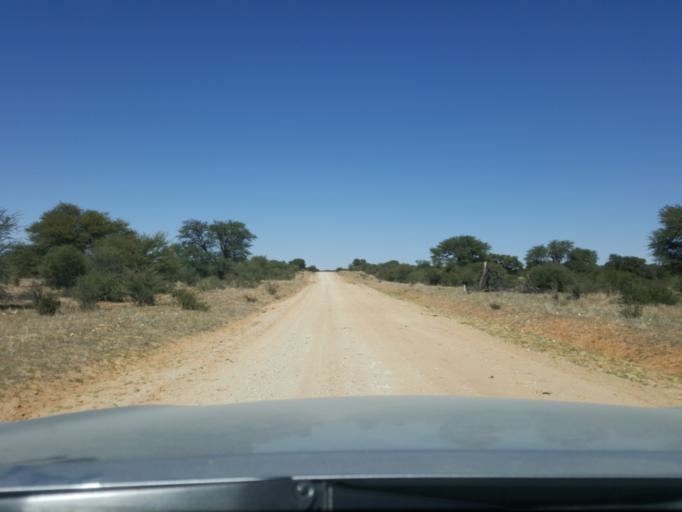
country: BW
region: Kgalagadi
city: Hukuntsi
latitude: -24.1102
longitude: 21.2336
